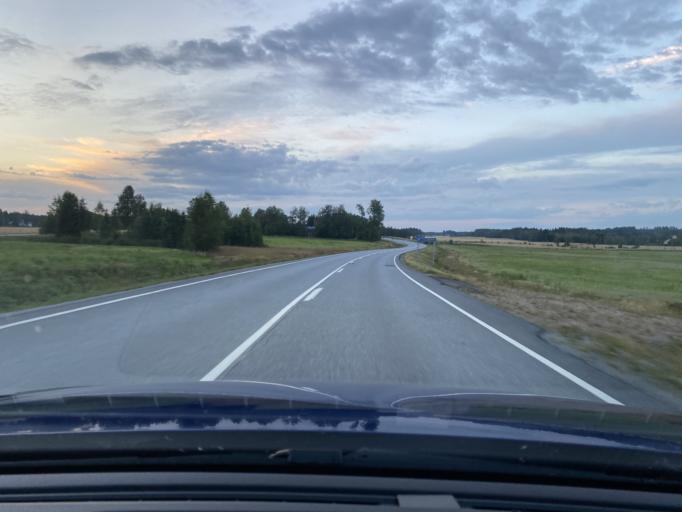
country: FI
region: Satakunta
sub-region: Pohjois-Satakunta
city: Honkajoki
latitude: 62.0970
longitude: 22.2432
